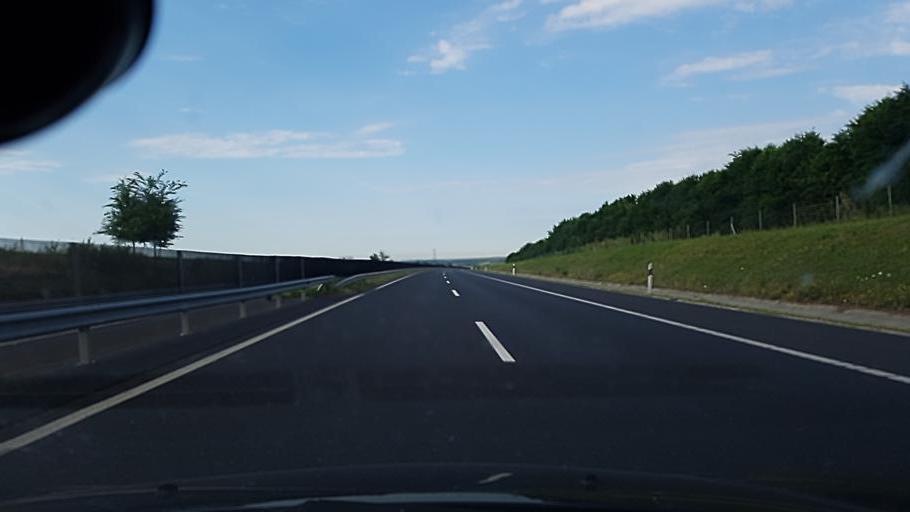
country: HU
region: Fejer
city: Rackeresztur
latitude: 47.2788
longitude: 18.8615
